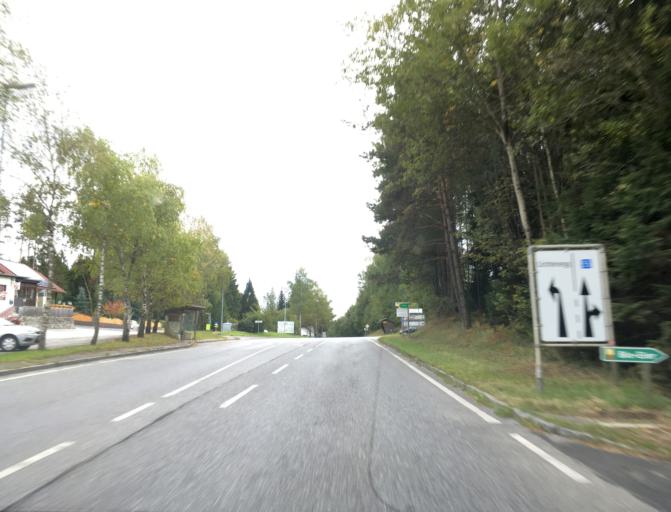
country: AT
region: Lower Austria
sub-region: Politischer Bezirk Neunkirchen
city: Thomasberg
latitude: 47.5416
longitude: 16.1551
